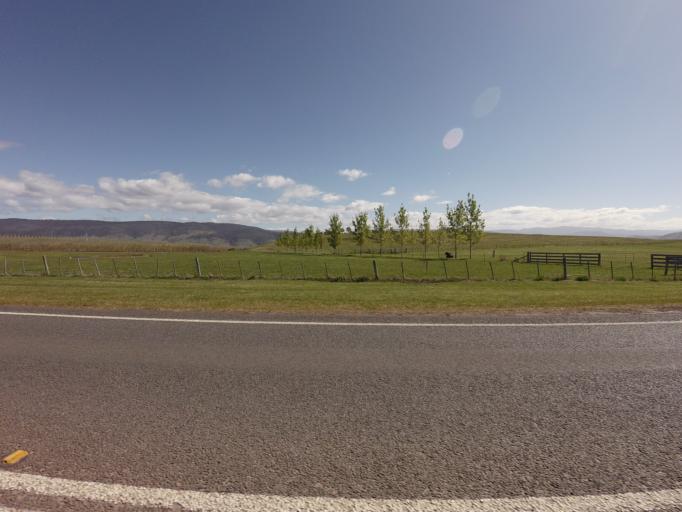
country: AU
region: Tasmania
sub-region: Derwent Valley
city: New Norfolk
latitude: -42.7050
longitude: 146.9436
